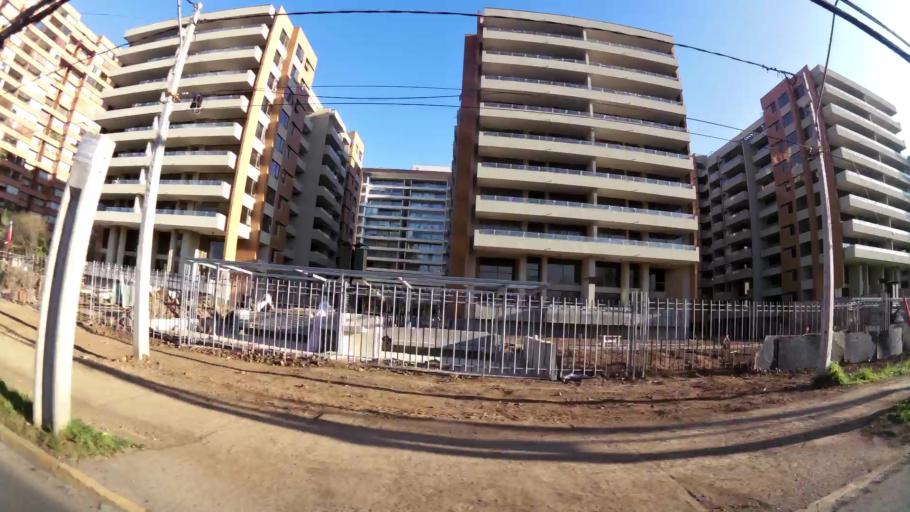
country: CL
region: Santiago Metropolitan
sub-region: Provincia de Santiago
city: Villa Presidente Frei, Nunoa, Santiago, Chile
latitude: -33.3979
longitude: -70.5636
